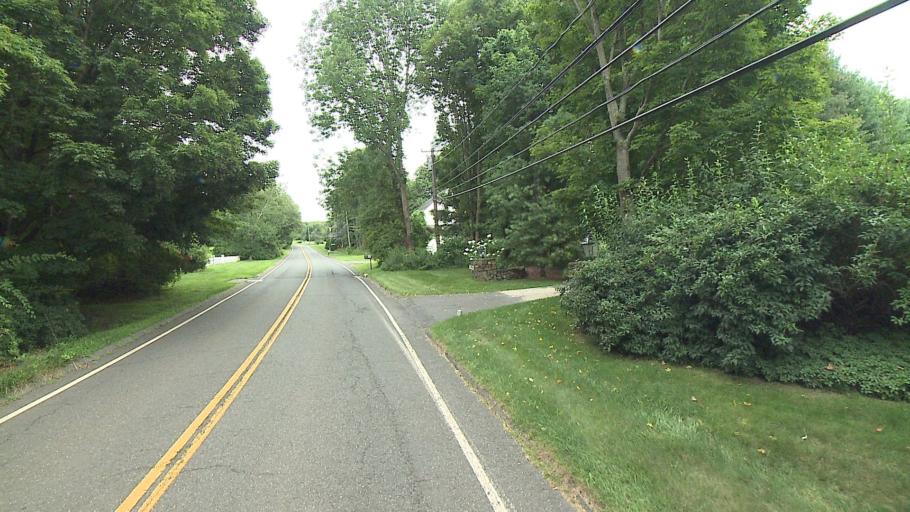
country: US
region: Connecticut
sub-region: Litchfield County
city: Woodbury
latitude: 41.5563
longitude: -73.2752
